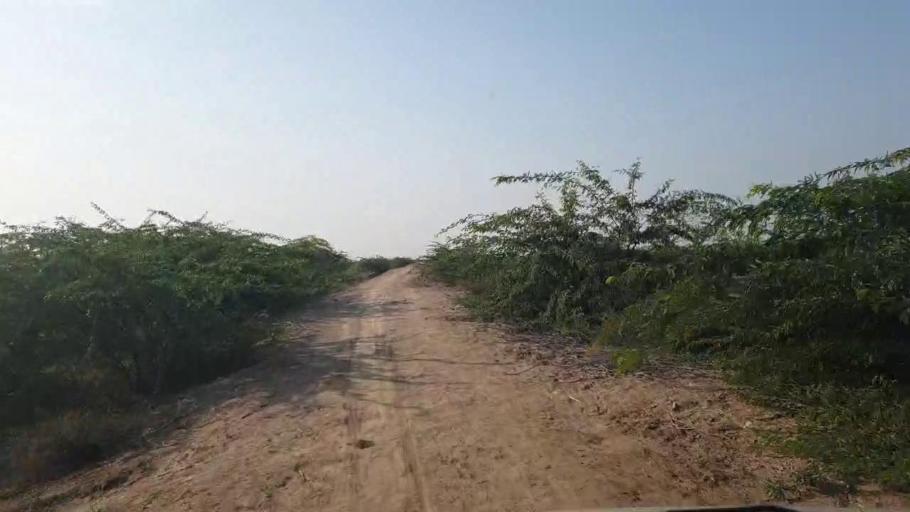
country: PK
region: Sindh
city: Badin
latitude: 24.4514
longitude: 68.7326
